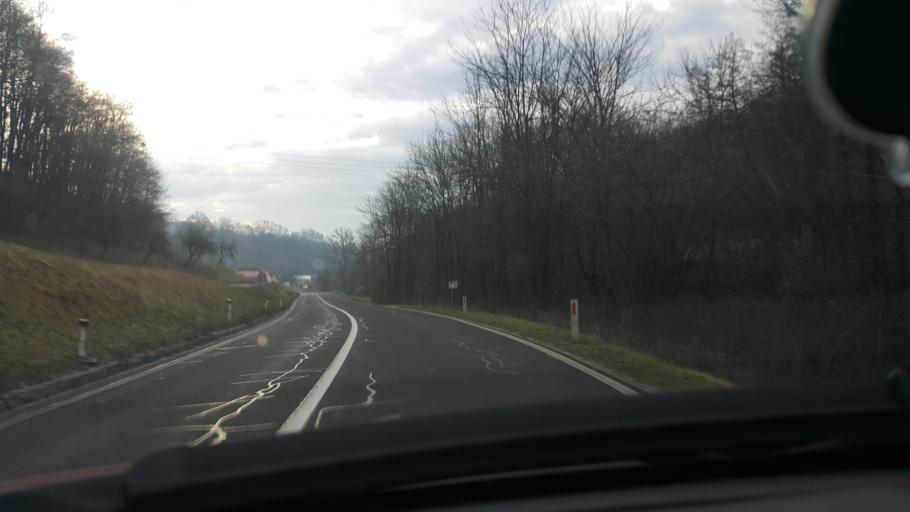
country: SI
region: Podcetrtek
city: Podcetrtek
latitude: 46.2113
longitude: 15.5857
